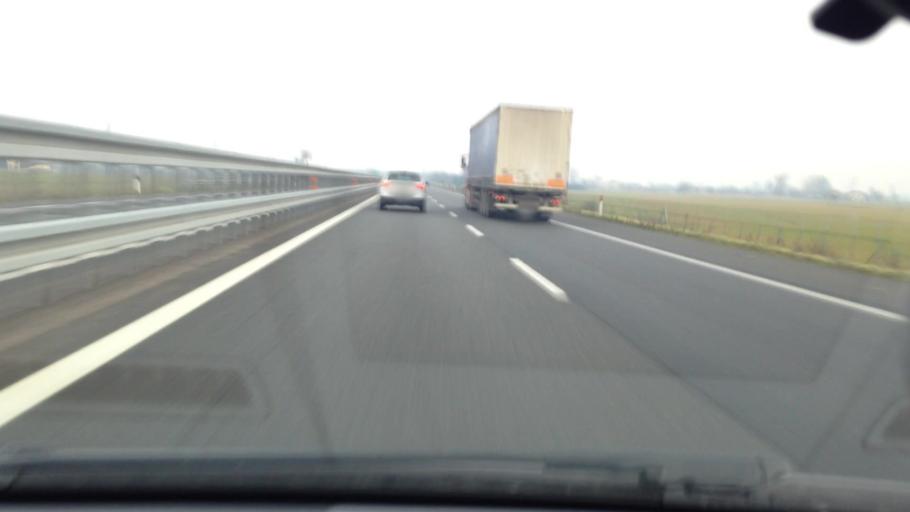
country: IT
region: Piedmont
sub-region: Provincia di Alessandria
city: Solero
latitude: 44.9299
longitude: 8.5271
